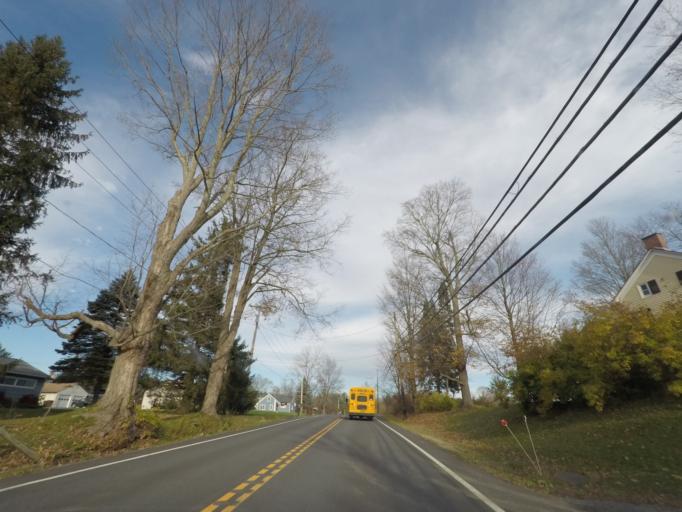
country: US
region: New York
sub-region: Albany County
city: Delmar
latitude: 42.6039
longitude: -73.8803
